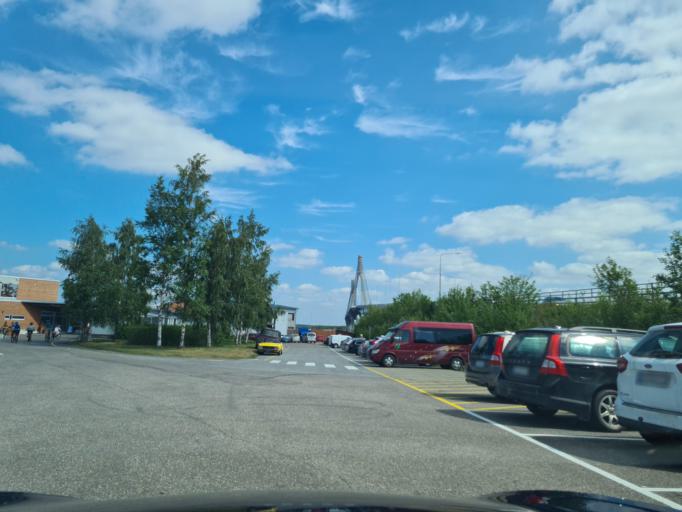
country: FI
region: Ostrobothnia
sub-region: Vaasa
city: Replot
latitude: 63.2069
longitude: 21.4603
